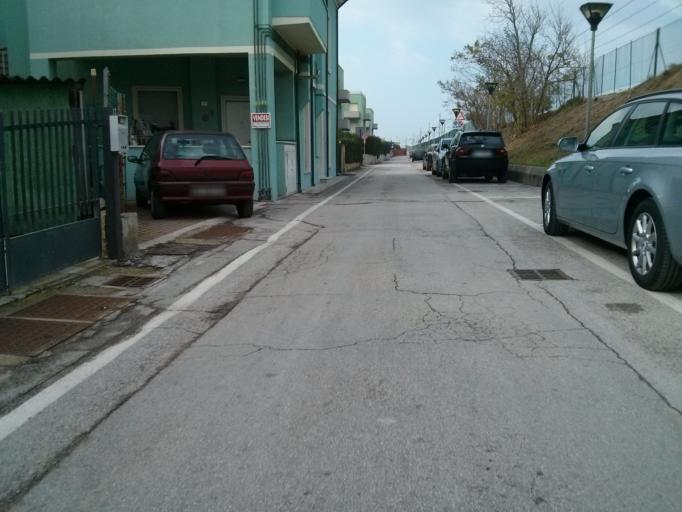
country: IT
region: The Marches
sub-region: Provincia di Pesaro e Urbino
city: Fano
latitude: 43.8524
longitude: 13.0073
